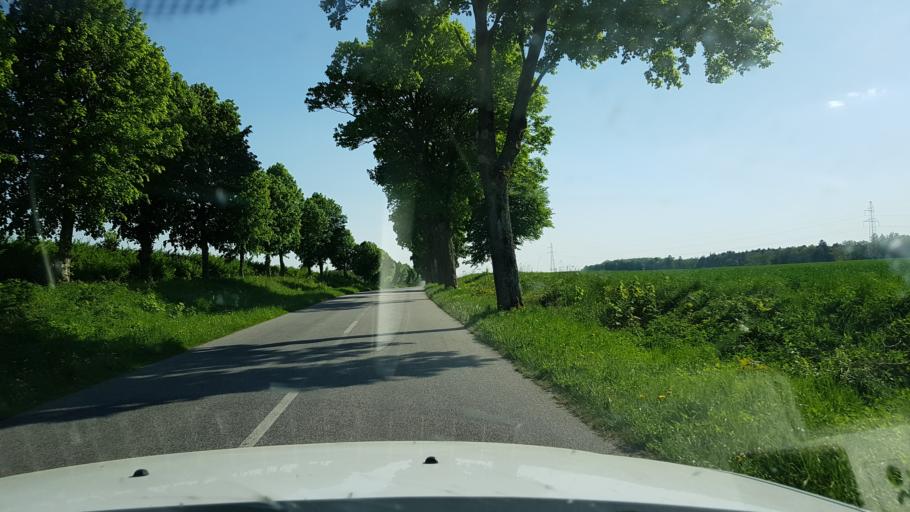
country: PL
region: West Pomeranian Voivodeship
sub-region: Powiat lobeski
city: Resko
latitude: 53.8051
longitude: 15.4184
